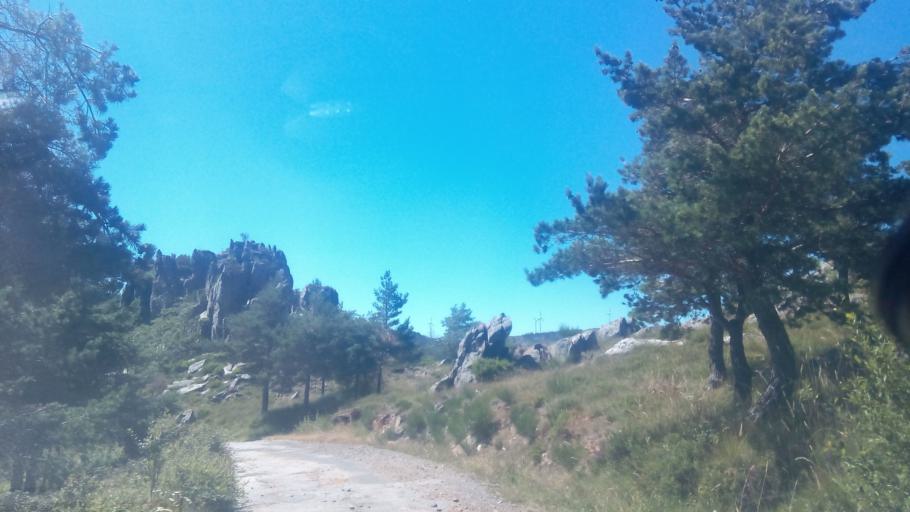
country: PT
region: Vila Real
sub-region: Mesao Frio
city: Mesao Frio
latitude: 41.2723
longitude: -7.9070
